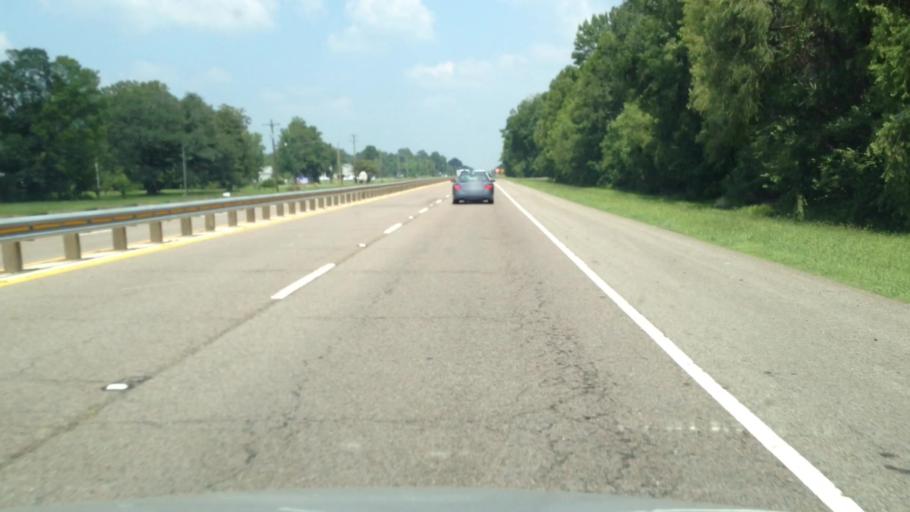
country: US
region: Louisiana
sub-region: Pointe Coupee Parish
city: Livonia
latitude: 30.5541
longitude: -91.5335
